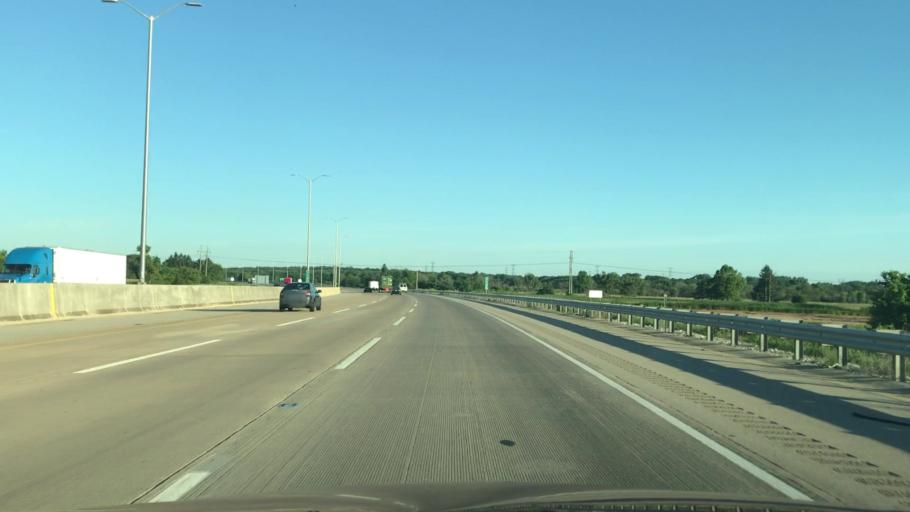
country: US
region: Illinois
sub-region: Winnebago County
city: Cherry Valley
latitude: 42.2443
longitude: -88.9245
